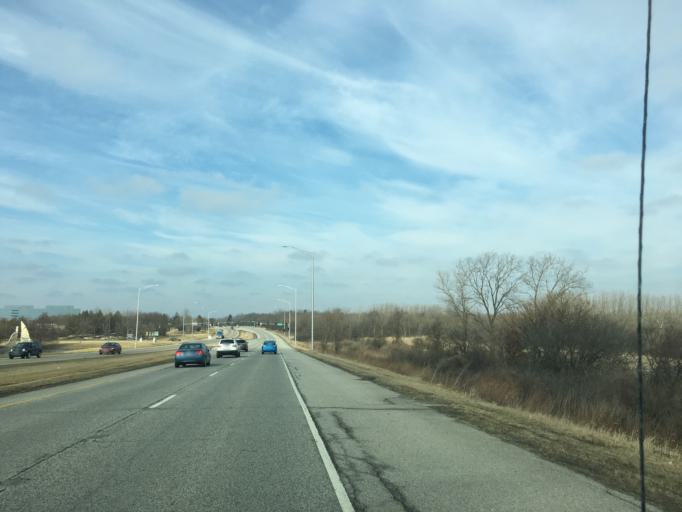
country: US
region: Illinois
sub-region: Cook County
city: Streamwood
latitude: 42.0783
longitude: -88.2026
